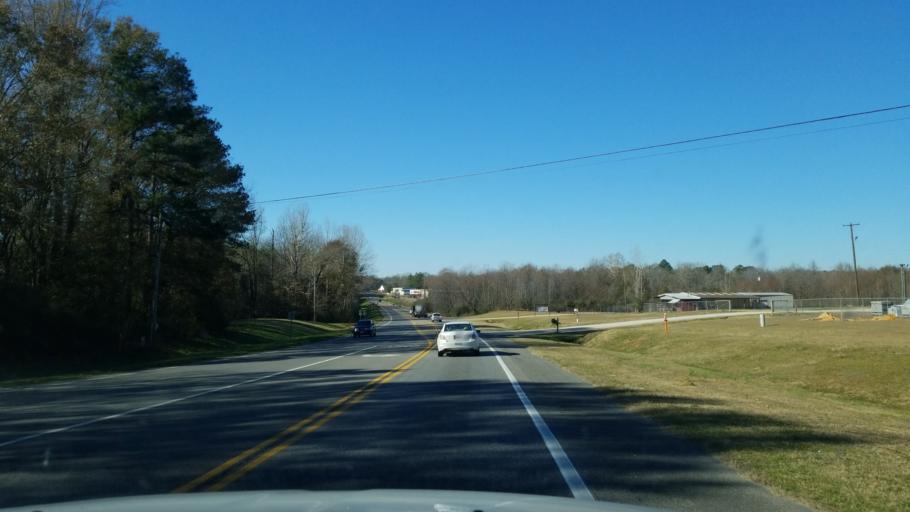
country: US
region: Alabama
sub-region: Pickens County
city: Gordo
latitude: 33.3135
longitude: -87.8945
